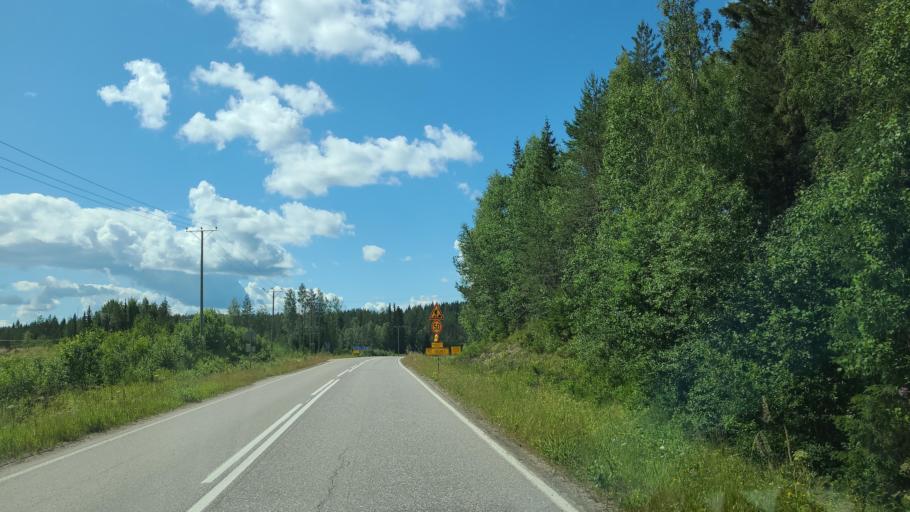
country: FI
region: Northern Savo
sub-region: Koillis-Savo
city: Kaavi
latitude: 62.9686
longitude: 28.7676
